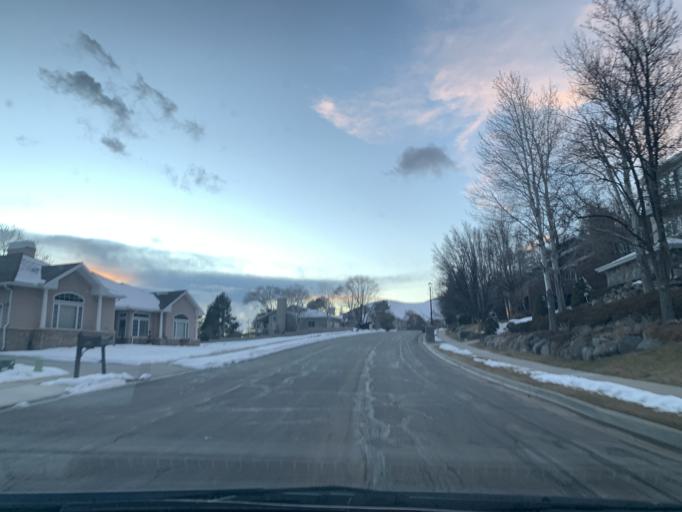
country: US
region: Utah
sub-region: Salt Lake County
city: Salt Lake City
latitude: 40.7838
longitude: -111.8500
